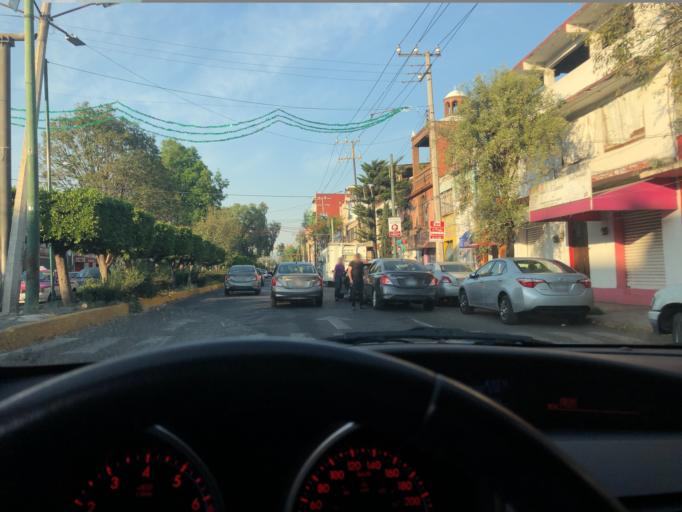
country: MX
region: Mexico City
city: Azcapotzalco
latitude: 19.4777
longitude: -99.1845
